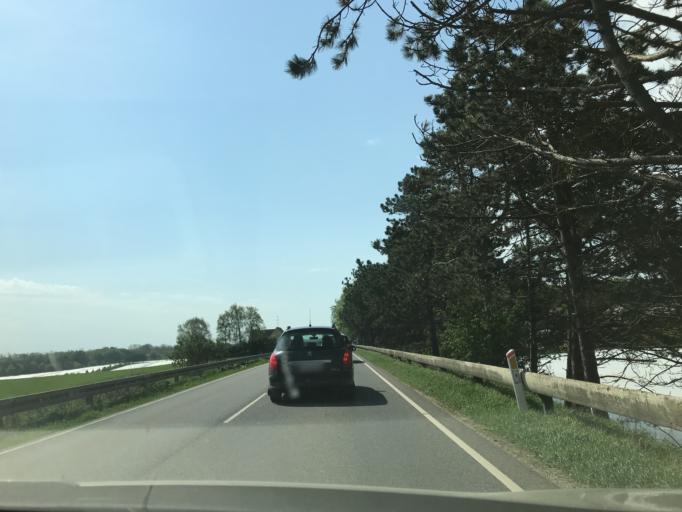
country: DK
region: South Denmark
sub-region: Assens Kommune
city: Assens
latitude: 55.3396
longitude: 9.9383
